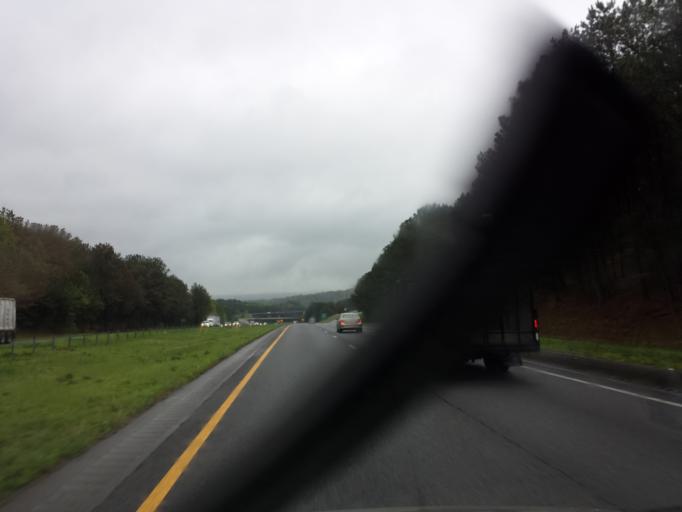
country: US
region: Georgia
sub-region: Cherokee County
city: Canton
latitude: 34.2123
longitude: -84.4915
